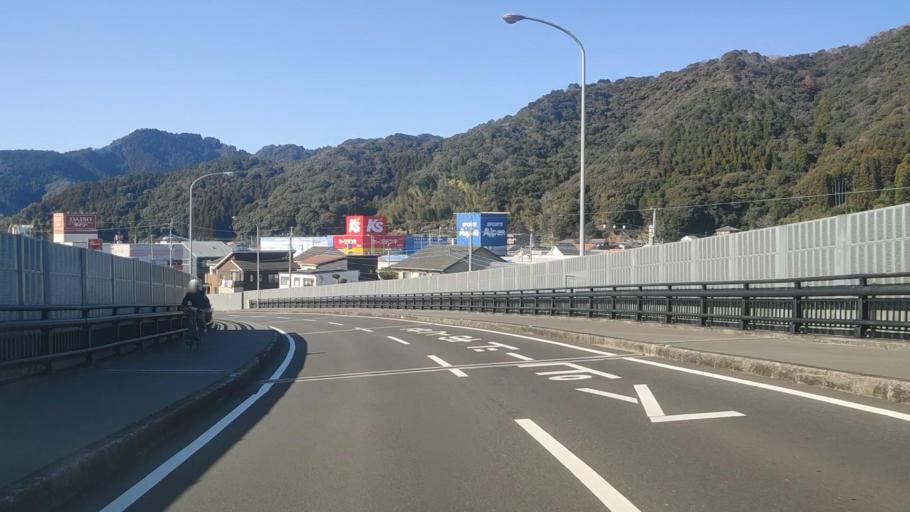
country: JP
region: Oita
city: Saiki
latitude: 32.9606
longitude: 131.8705
